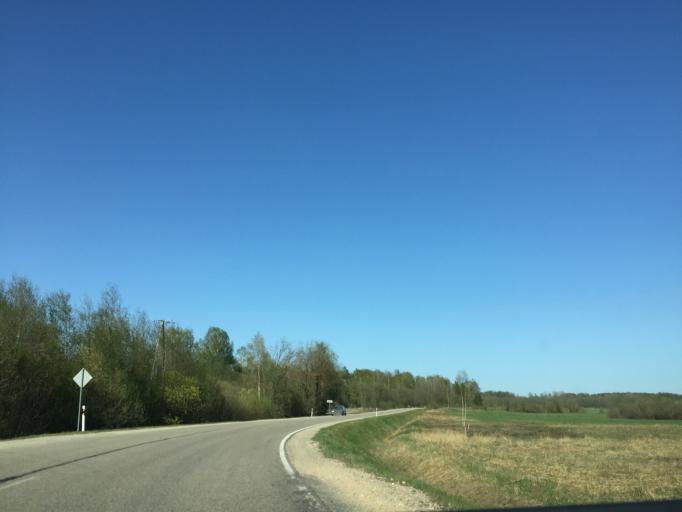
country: LV
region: Ergli
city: Ergli
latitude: 56.9000
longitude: 25.4219
